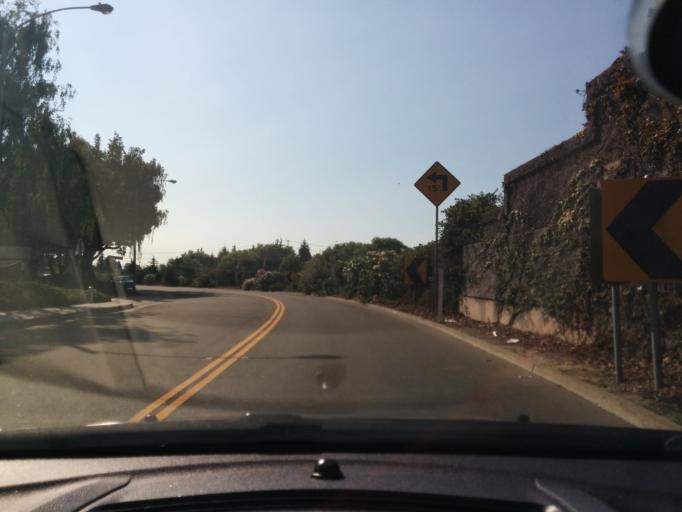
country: US
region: California
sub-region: Santa Clara County
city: Sunnyvale
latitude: 37.3949
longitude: -122.0104
